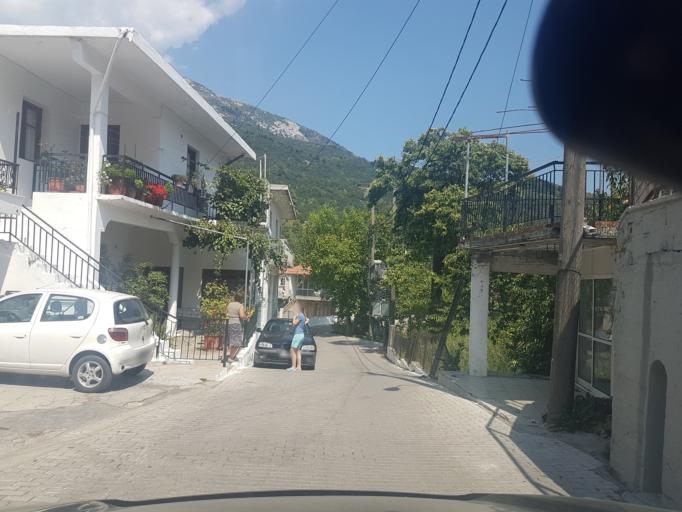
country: GR
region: Central Greece
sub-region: Nomos Evvoias
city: Yimnon
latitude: 38.6183
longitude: 23.8898
